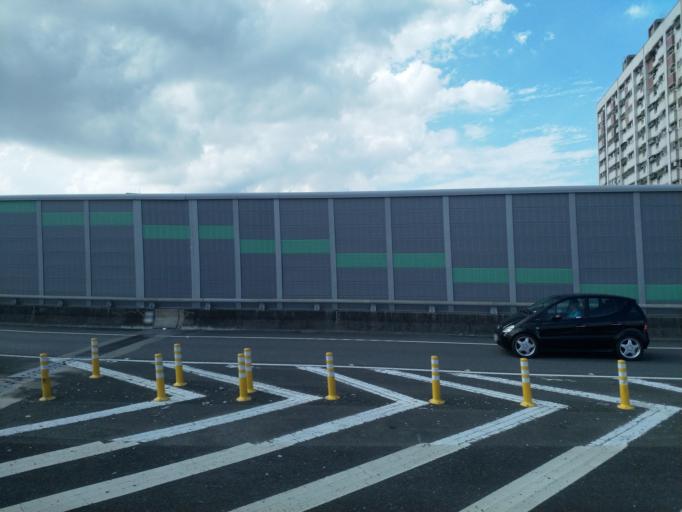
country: TW
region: Taiwan
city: Fengshan
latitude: 22.6754
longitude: 120.3261
